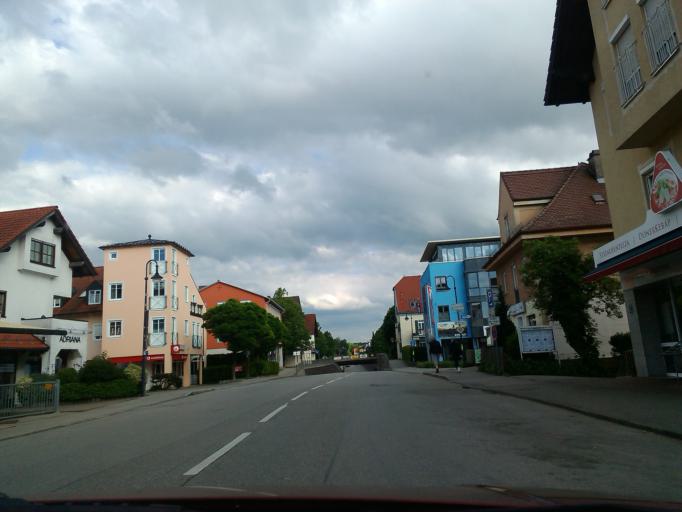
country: DE
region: Bavaria
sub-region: Upper Bavaria
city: Gilching
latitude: 48.1083
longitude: 11.3011
